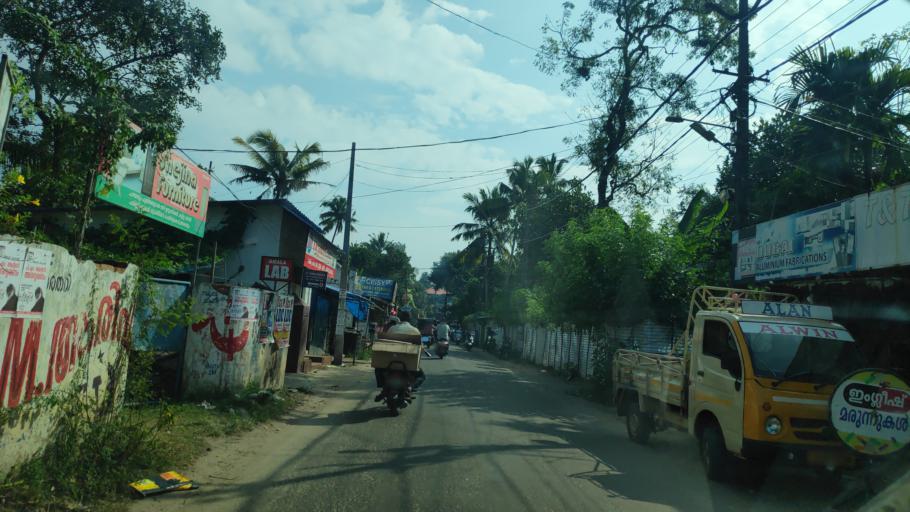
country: IN
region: Kerala
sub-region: Alappuzha
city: Alleppey
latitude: 9.5074
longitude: 76.3203
